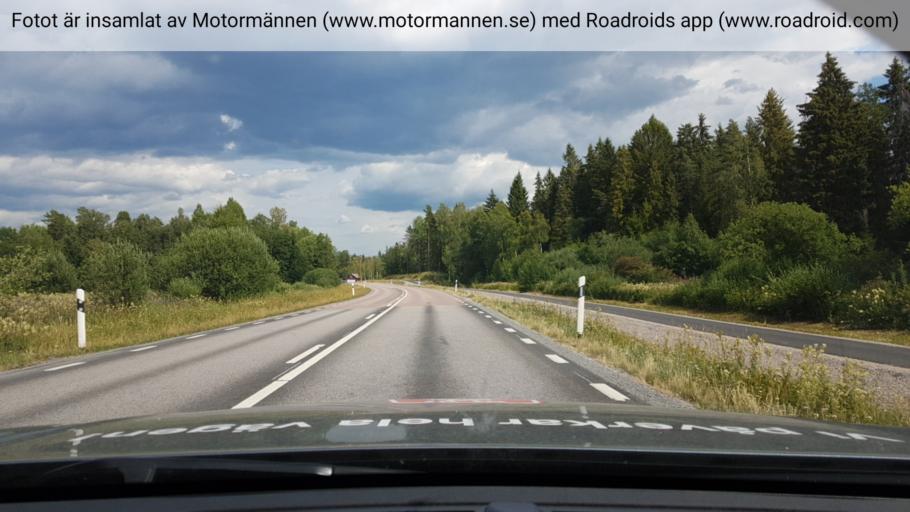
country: SE
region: Uppsala
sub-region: Heby Kommun
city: Morgongava
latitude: 59.9357
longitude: 16.9292
